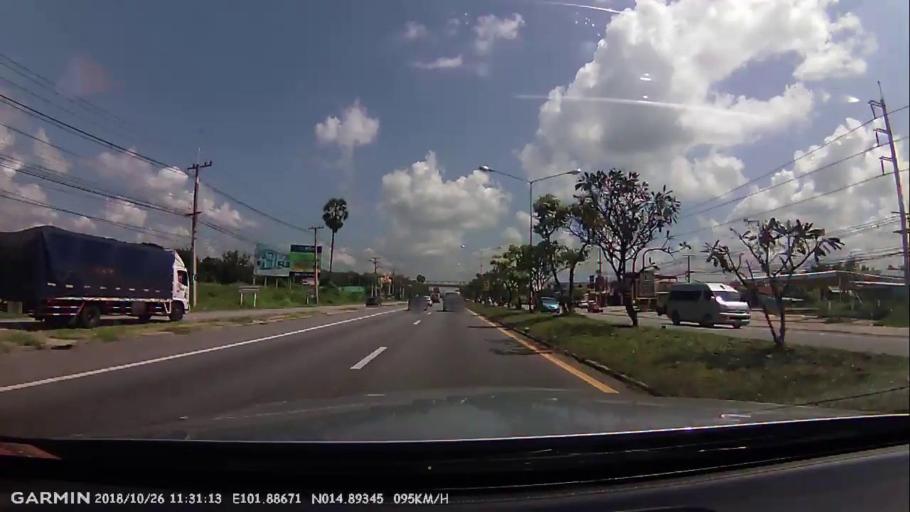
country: TH
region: Nakhon Ratchasima
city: Sung Noen
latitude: 14.8937
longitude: 101.8865
